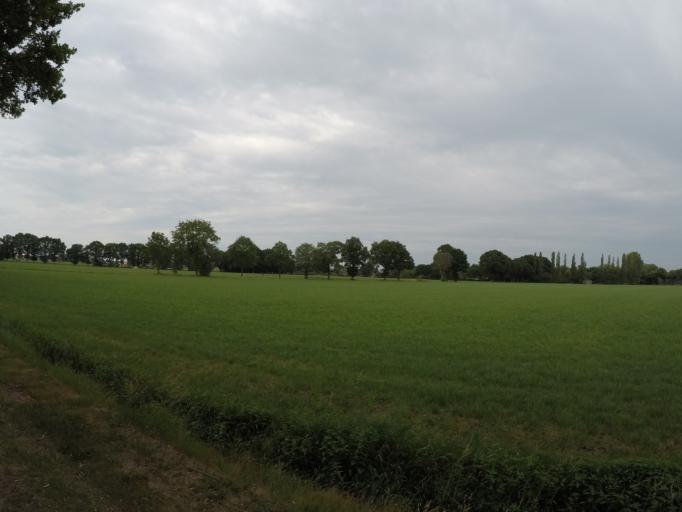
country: BE
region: Flanders
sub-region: Provincie Antwerpen
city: Kalmthout
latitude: 51.4175
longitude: 4.4847
